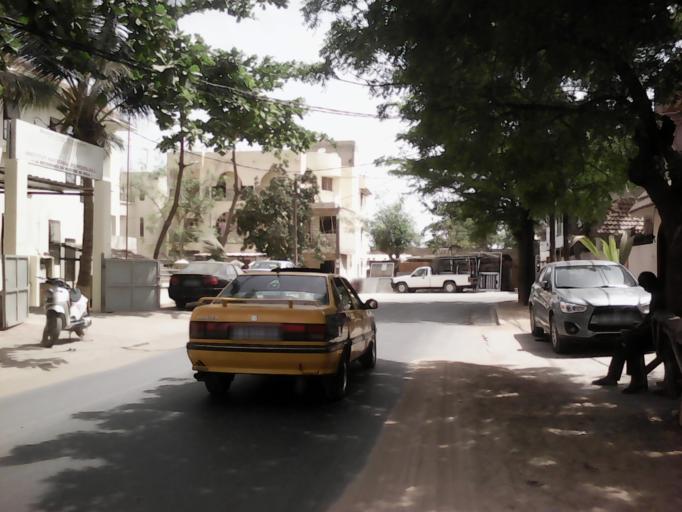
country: SN
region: Dakar
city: Grand Dakar
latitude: 14.7326
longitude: -17.4317
